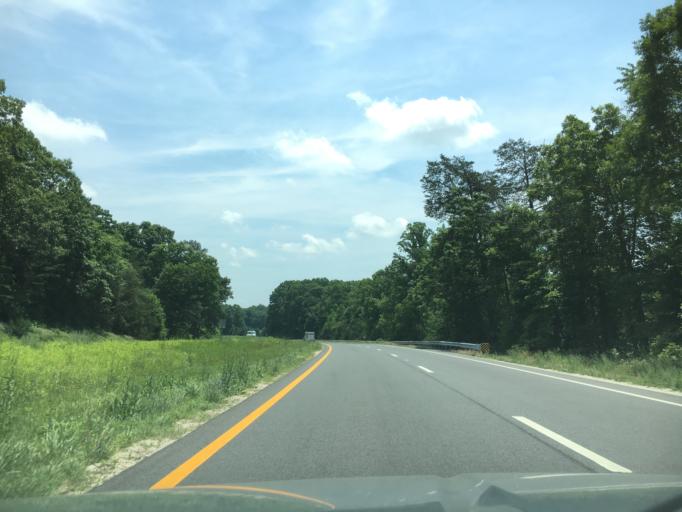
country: US
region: Virginia
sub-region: Campbell County
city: Concord
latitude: 37.3536
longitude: -78.9971
